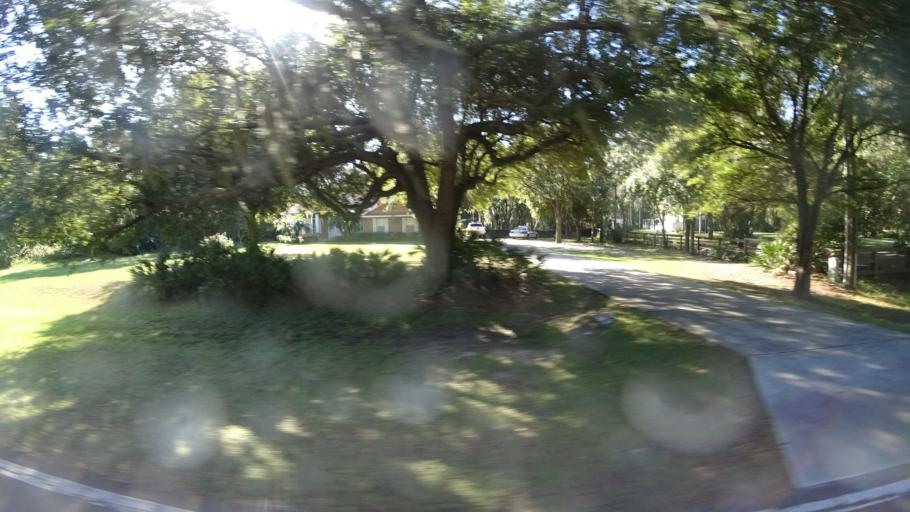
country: US
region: Florida
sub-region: Hillsborough County
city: Ruskin
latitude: 27.6490
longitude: -82.3990
